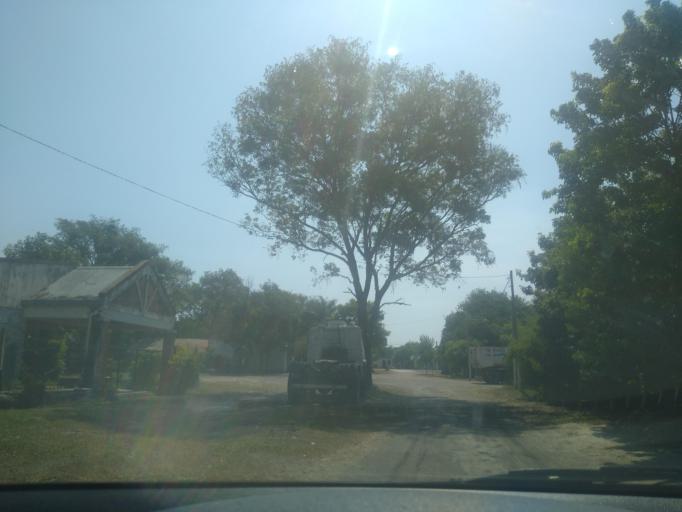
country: AR
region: Chaco
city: Puerto Tirol
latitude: -27.5609
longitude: -59.3052
